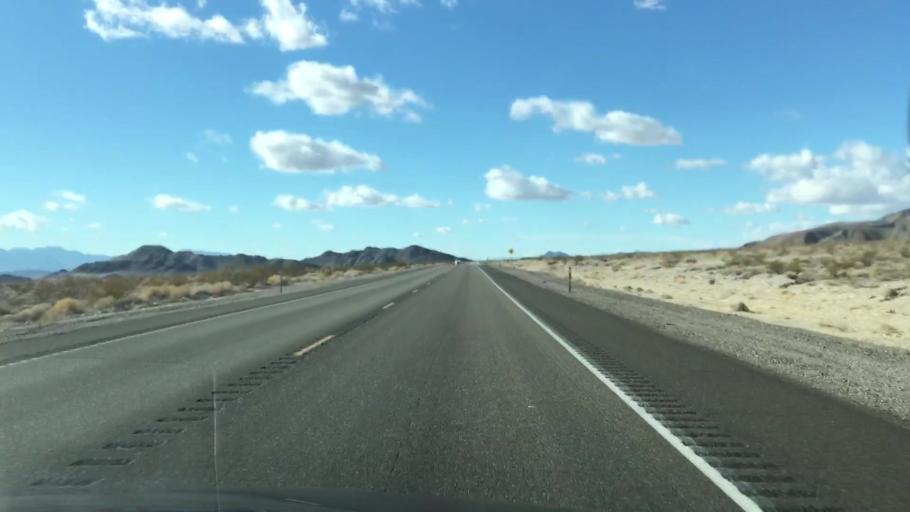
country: US
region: Nevada
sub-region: Nye County
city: Pahrump
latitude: 36.5724
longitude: -116.1767
